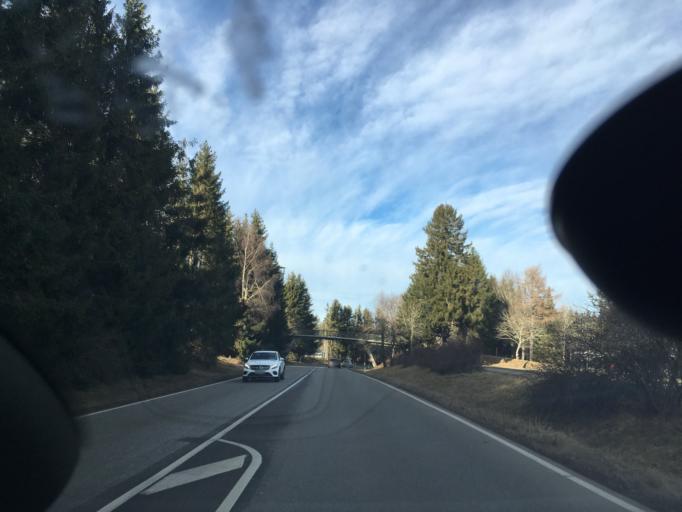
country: DE
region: Baden-Wuerttemberg
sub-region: Freiburg Region
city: Hochenschwand
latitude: 47.7353
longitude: 8.1619
